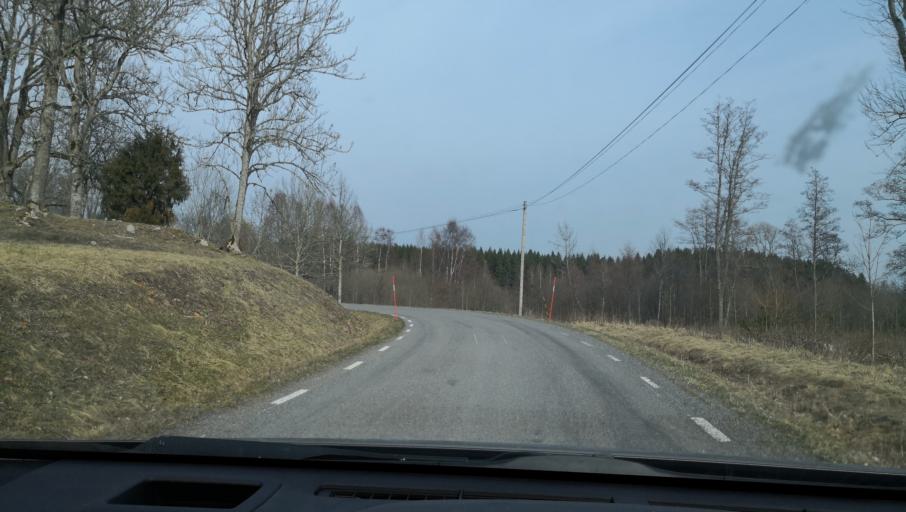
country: SE
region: OErebro
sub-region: Lindesbergs Kommun
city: Frovi
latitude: 59.4037
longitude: 15.4161
